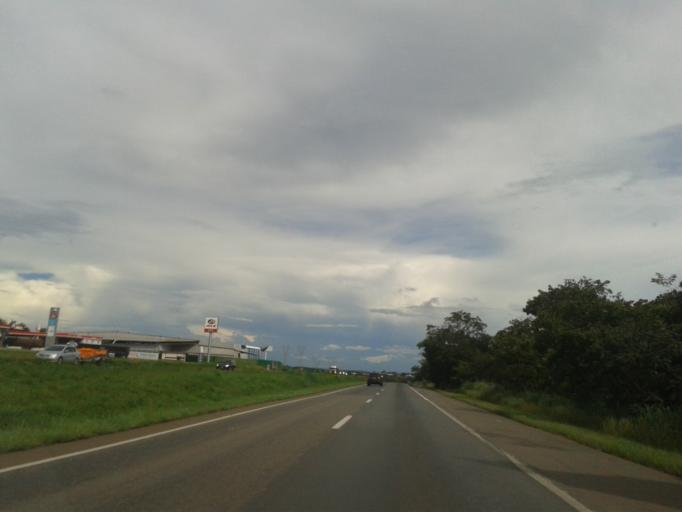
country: BR
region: Goias
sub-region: Hidrolandia
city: Hidrolandia
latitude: -16.9481
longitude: -49.2488
